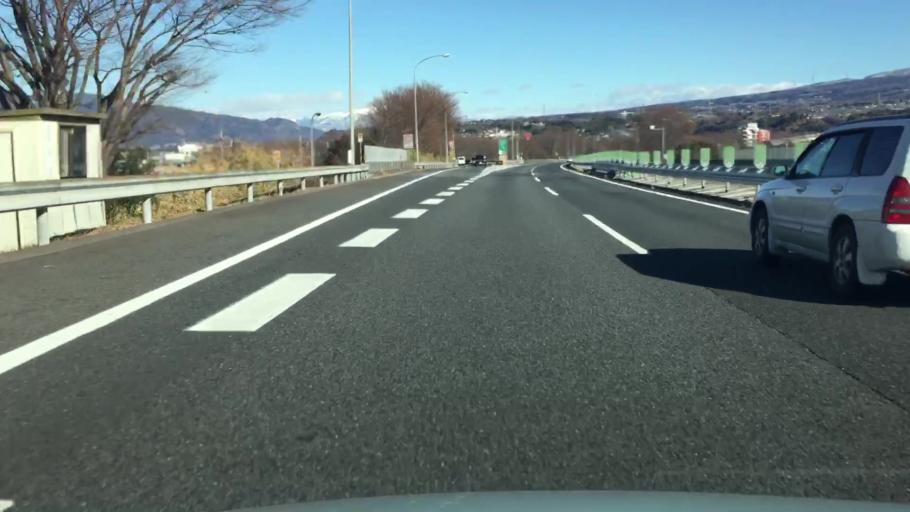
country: JP
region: Gunma
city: Shibukawa
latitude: 36.4728
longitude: 139.0136
